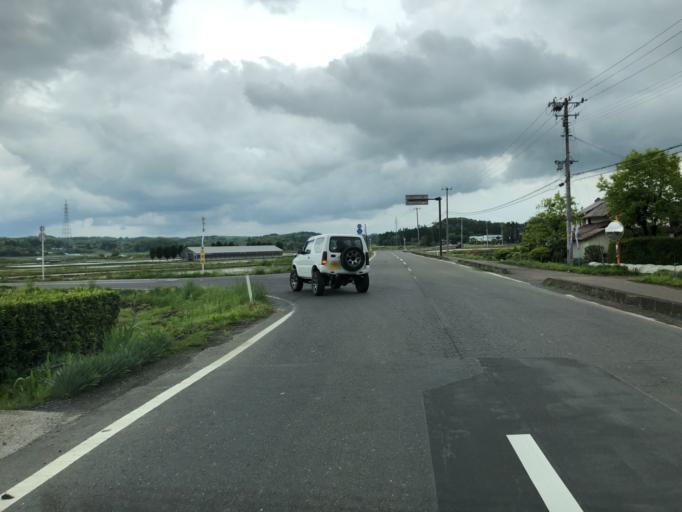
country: JP
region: Fukushima
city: Ishikawa
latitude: 37.1891
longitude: 140.3941
